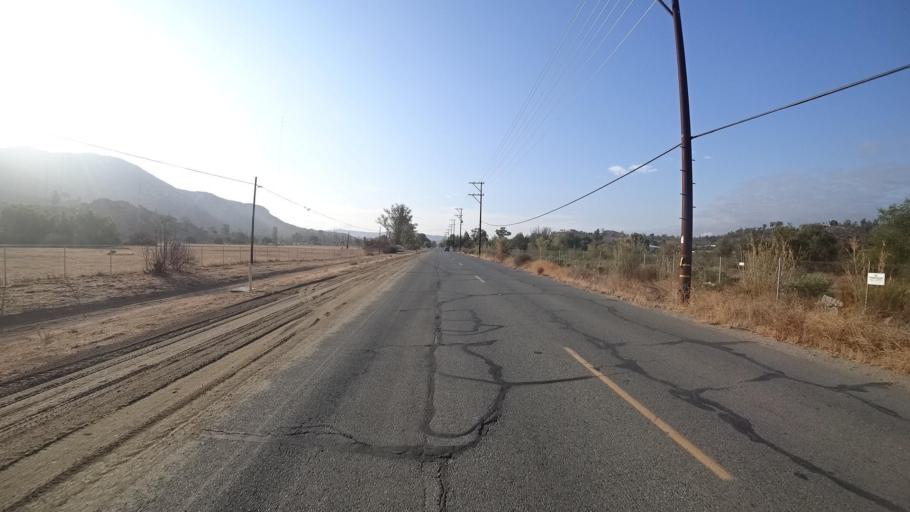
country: US
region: California
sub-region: San Diego County
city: Eucalyptus Hills
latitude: 32.8960
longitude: -116.9290
